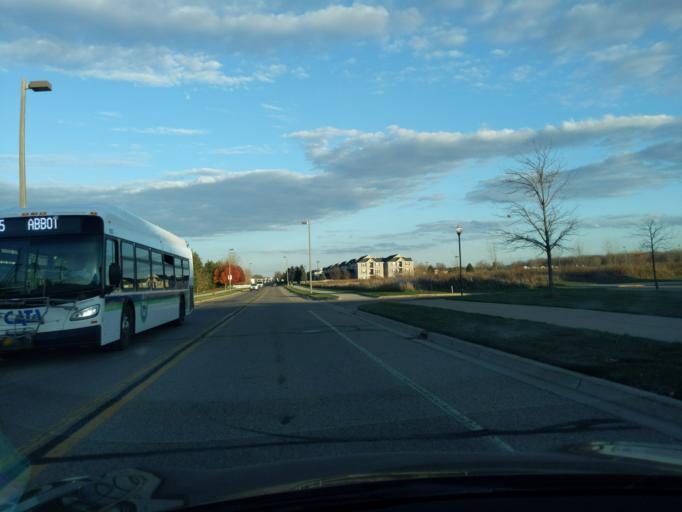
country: US
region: Michigan
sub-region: Ingham County
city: East Lansing
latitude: 42.7730
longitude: -84.4962
